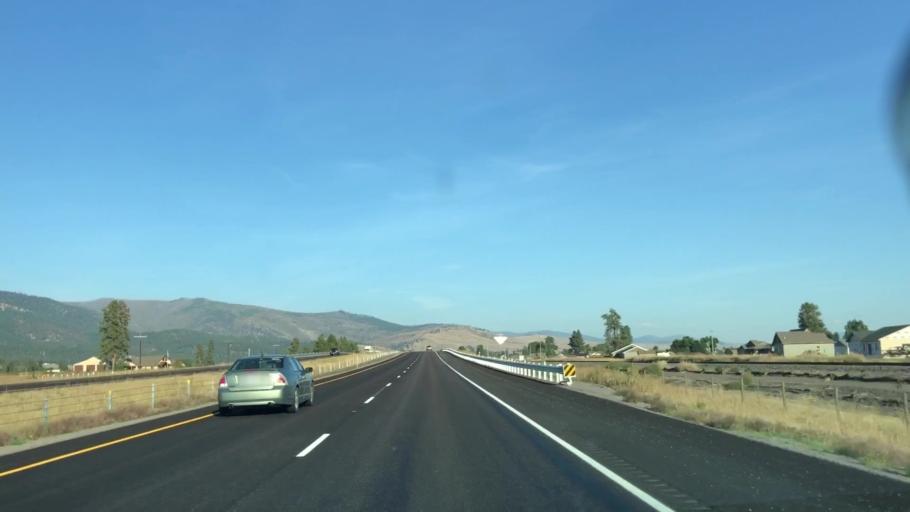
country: US
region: Montana
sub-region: Missoula County
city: Frenchtown
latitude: 47.0276
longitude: -114.2977
